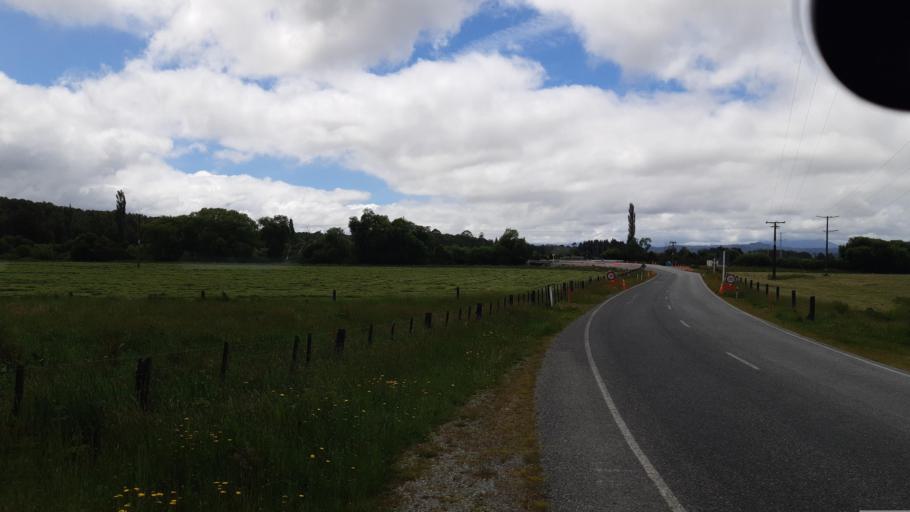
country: NZ
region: West Coast
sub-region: Grey District
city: Greymouth
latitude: -42.3377
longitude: 171.4727
